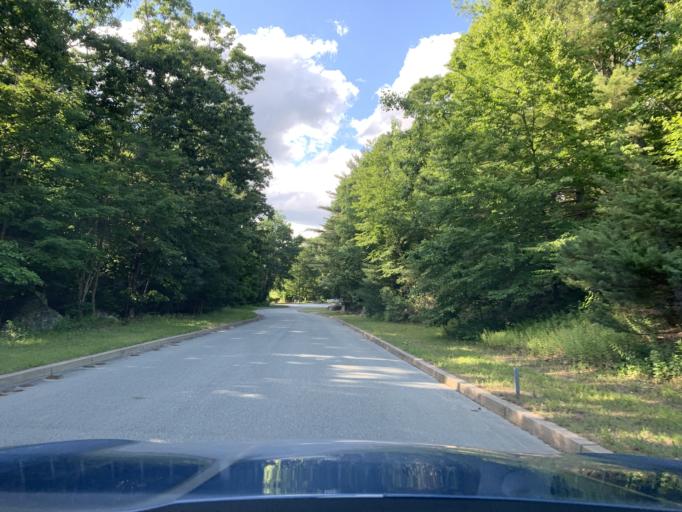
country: US
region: Rhode Island
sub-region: Kent County
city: West Warwick
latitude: 41.6592
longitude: -71.5235
